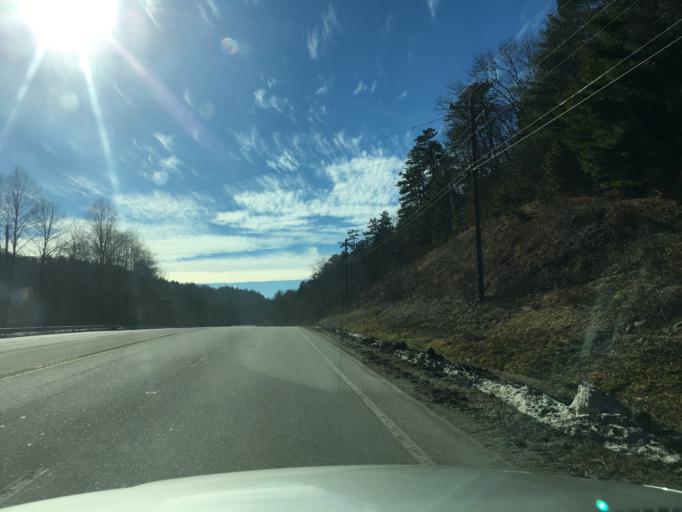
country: US
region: North Carolina
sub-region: Henderson County
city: Etowah
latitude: 35.3063
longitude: -82.6692
